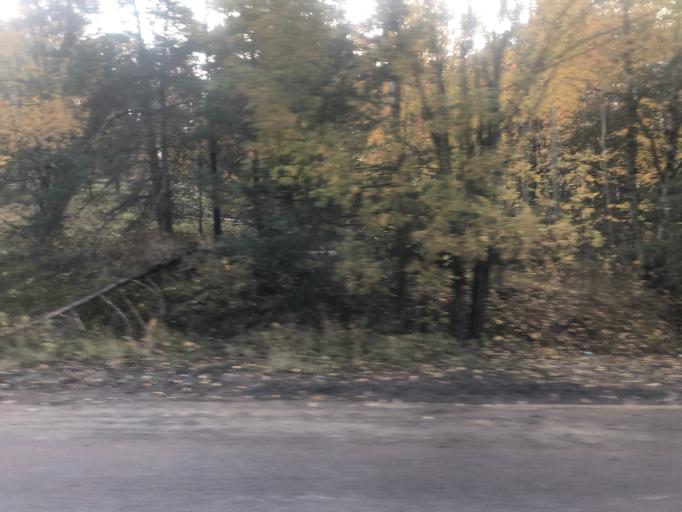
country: SE
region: Stockholm
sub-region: Jarfalla Kommun
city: Jakobsberg
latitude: 59.4058
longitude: 17.8459
